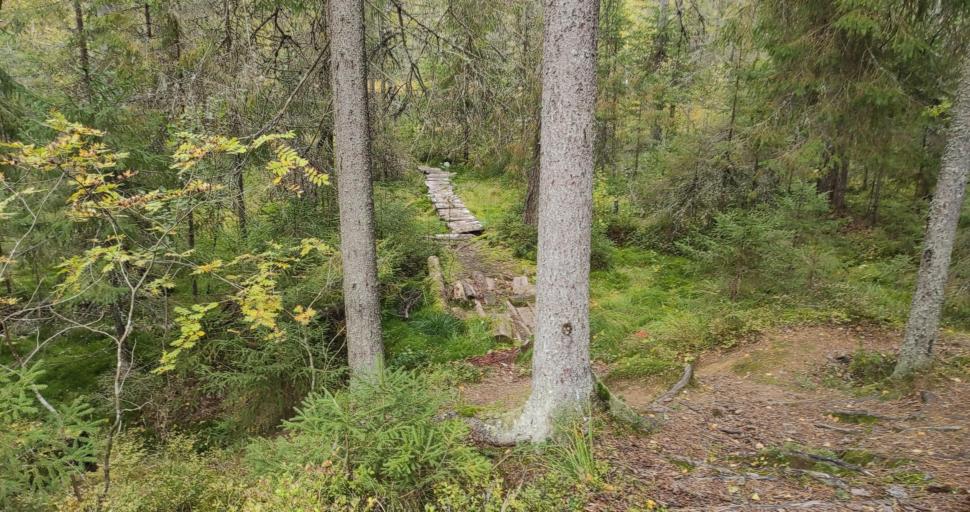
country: RU
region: Leningrad
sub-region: Vsevolzhskij Rajon
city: Vaskelovo
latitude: 60.4200
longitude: 30.2960
